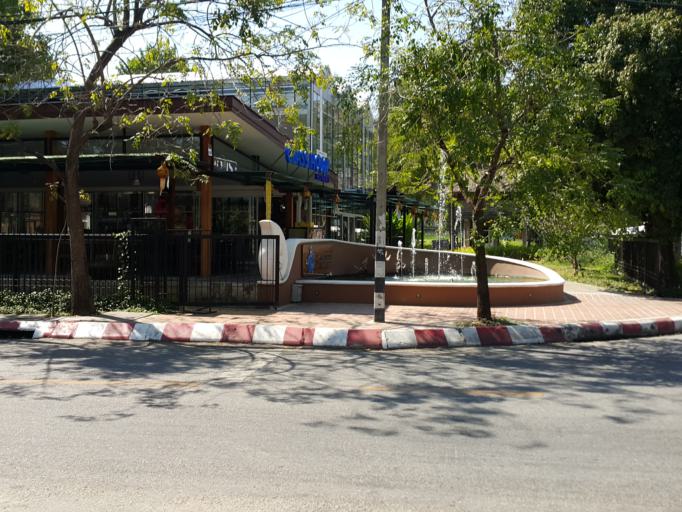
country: TH
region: Chiang Mai
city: Chiang Mai
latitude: 18.7932
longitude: 98.9901
